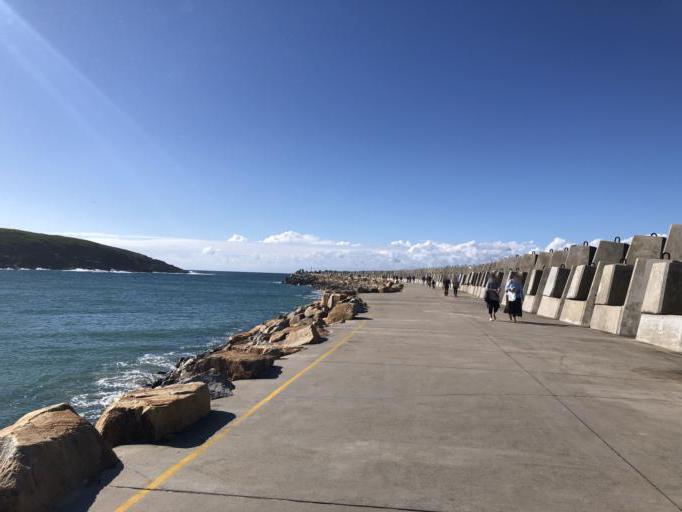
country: AU
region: New South Wales
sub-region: Coffs Harbour
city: Coffs Harbour
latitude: -30.3116
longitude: 153.1501
